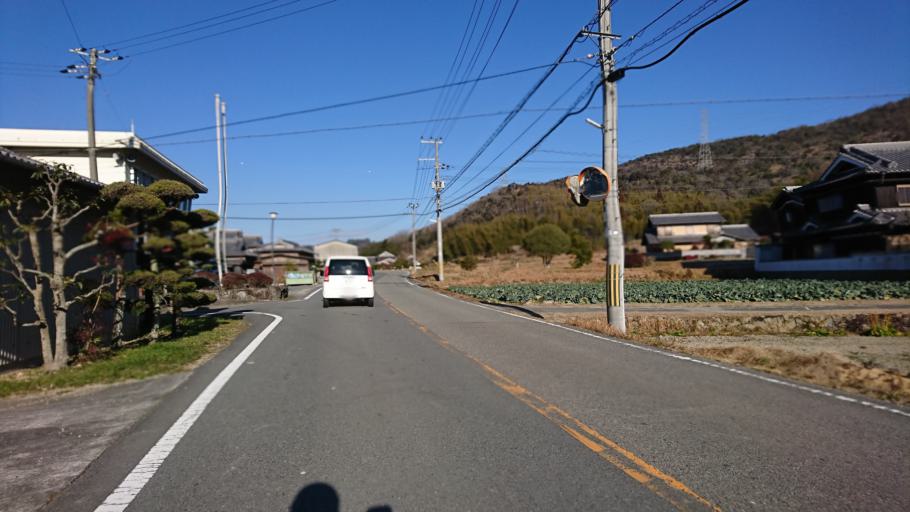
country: JP
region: Hyogo
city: Ono
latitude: 34.8406
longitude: 134.8637
